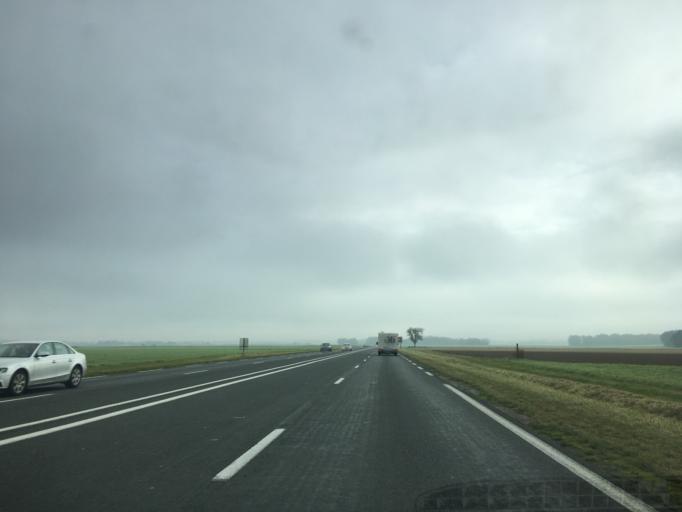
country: FR
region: Ile-de-France
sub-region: Departement de Seine-et-Marne
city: Perthes
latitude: 48.4628
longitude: 2.5593
